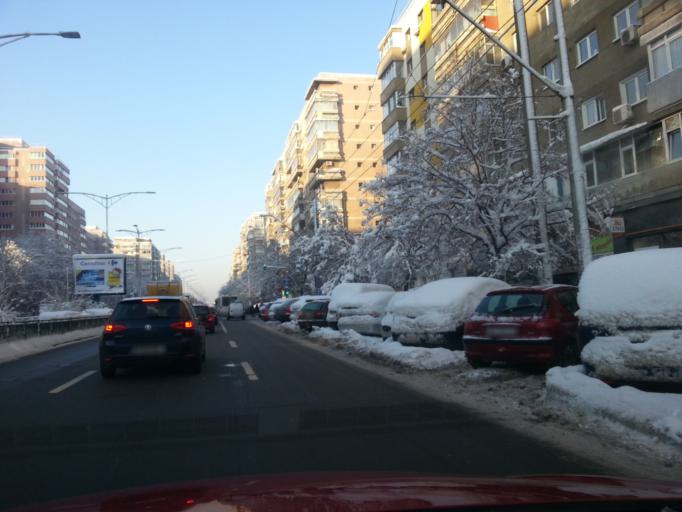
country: RO
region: Ilfov
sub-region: Comuna Chiajna
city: Rosu
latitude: 44.4340
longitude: 26.0165
